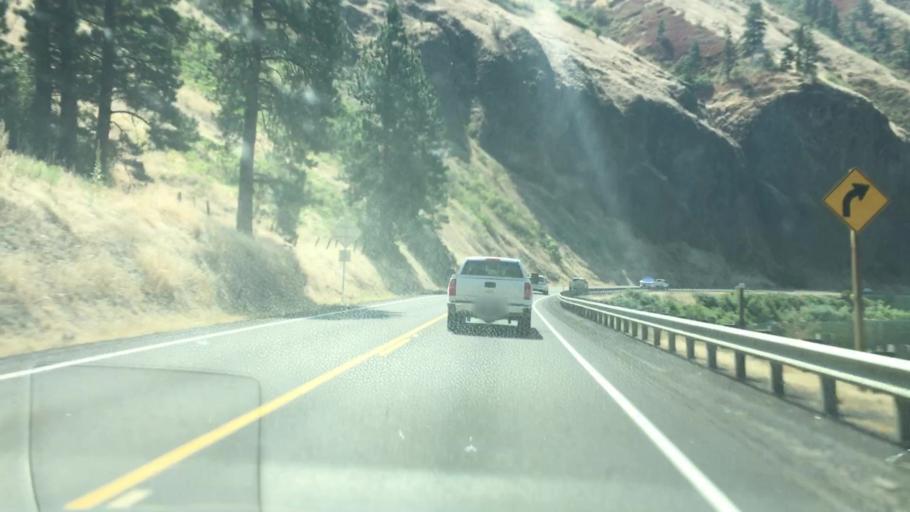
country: US
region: Idaho
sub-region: Nez Perce County
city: Lapwai
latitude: 46.4958
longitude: -116.7253
